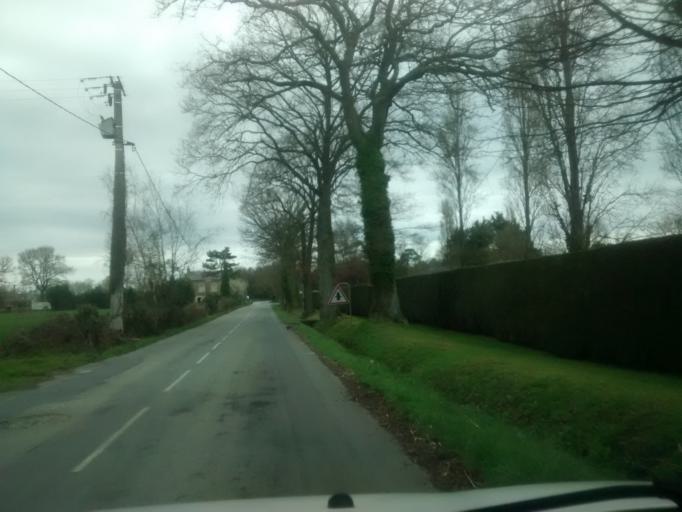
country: FR
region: Brittany
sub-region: Departement d'Ille-et-Vilaine
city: Fouillard
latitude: 48.1747
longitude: -1.6036
